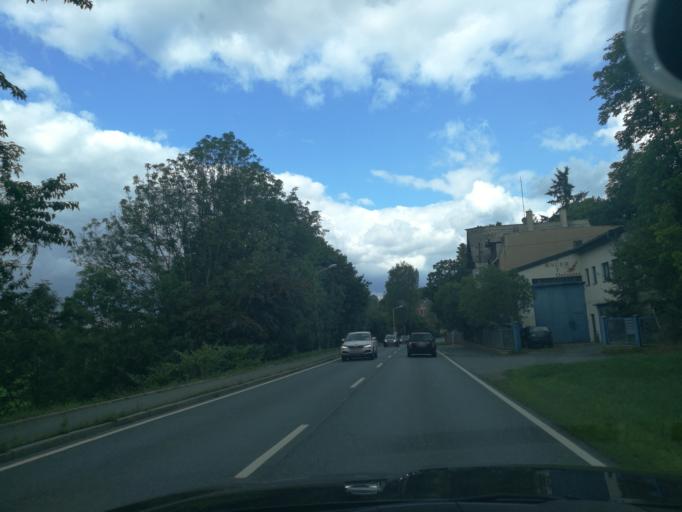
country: DE
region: Saxony
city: Oelsnitz
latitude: 50.4080
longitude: 12.1807
